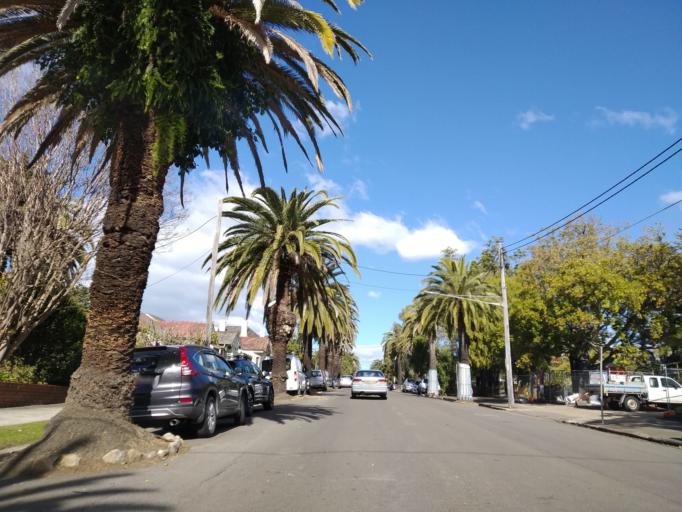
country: AU
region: New South Wales
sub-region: Ashfield
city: Summer Hill
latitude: -33.8943
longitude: 151.1299
